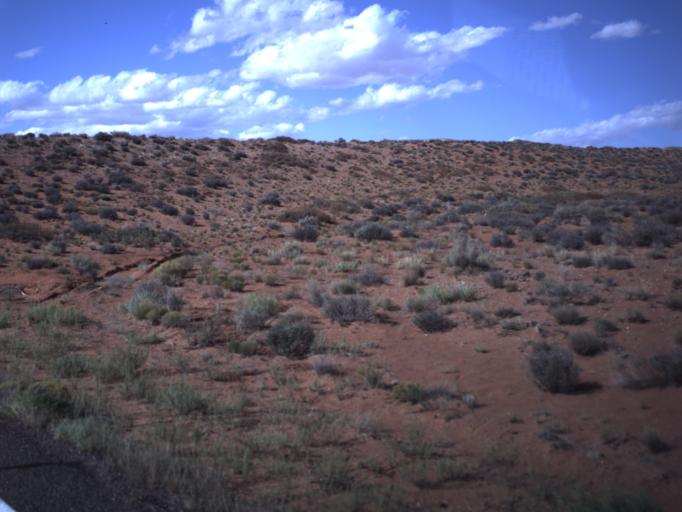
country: US
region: Utah
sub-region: Wayne County
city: Loa
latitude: 38.0681
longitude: -110.6047
